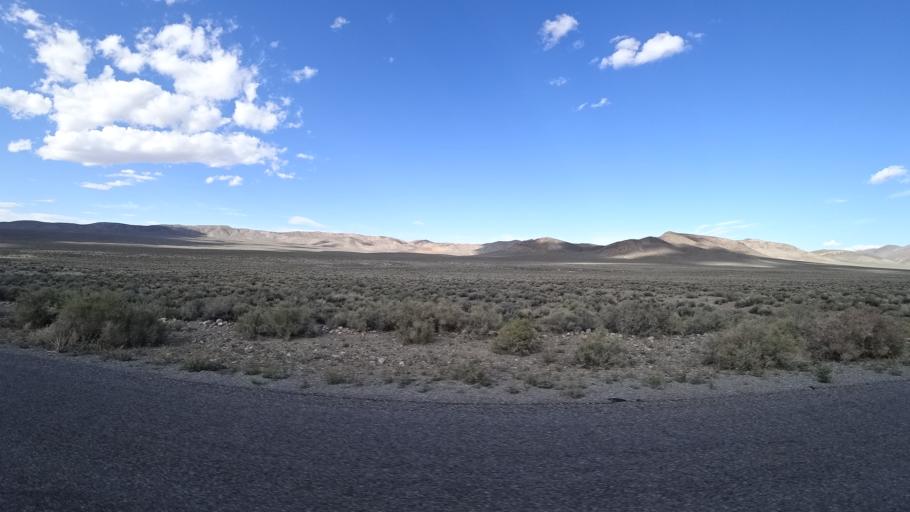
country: US
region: Nevada
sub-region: Nye County
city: Beatty
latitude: 36.3782
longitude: -117.1438
